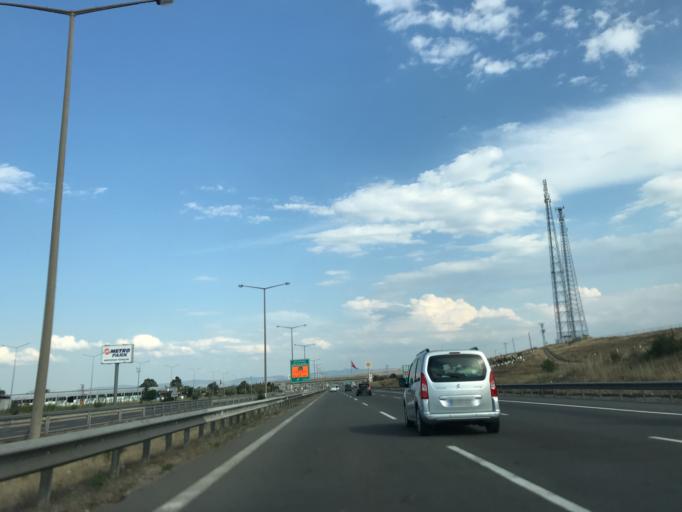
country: TR
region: Bolu
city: Dortdivan
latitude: 40.7529
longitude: 32.0752
